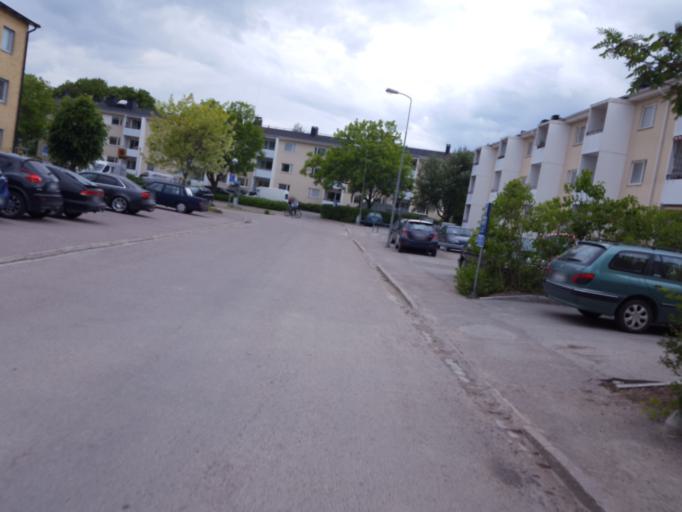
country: SE
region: Uppsala
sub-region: Uppsala Kommun
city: Uppsala
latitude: 59.8712
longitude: 17.6618
